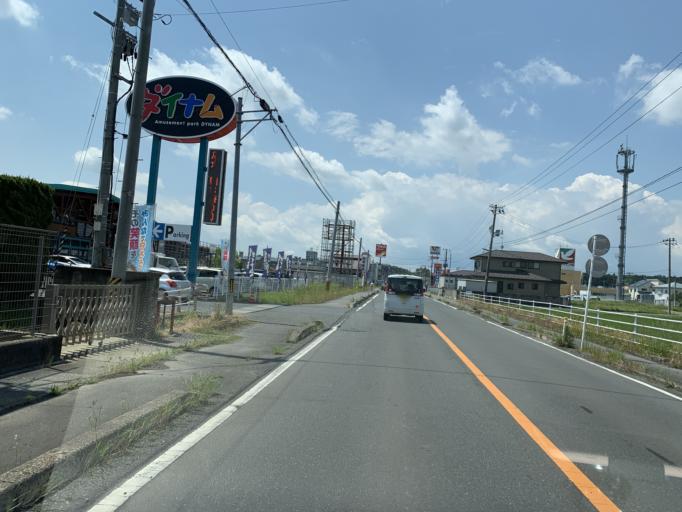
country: JP
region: Miyagi
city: Kogota
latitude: 38.5451
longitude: 141.0605
